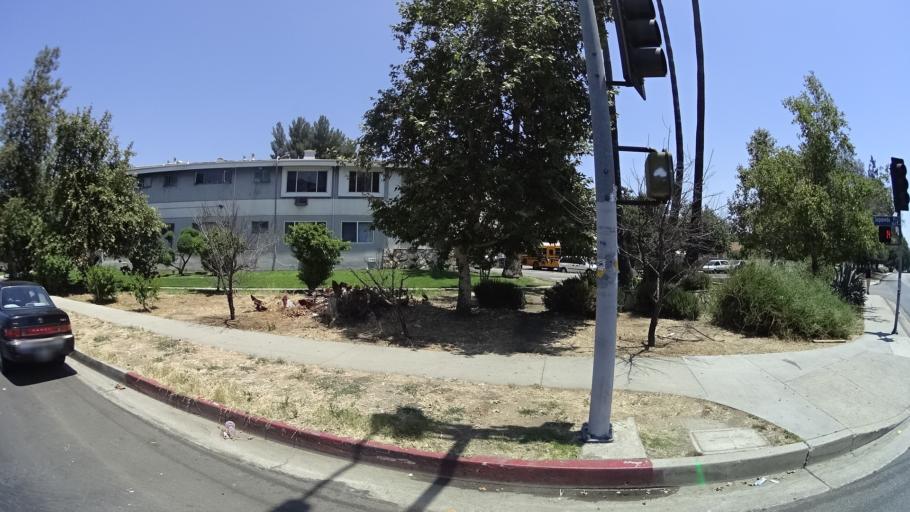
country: US
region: California
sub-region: Los Angeles County
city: Van Nuys
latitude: 34.2182
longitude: -118.4663
